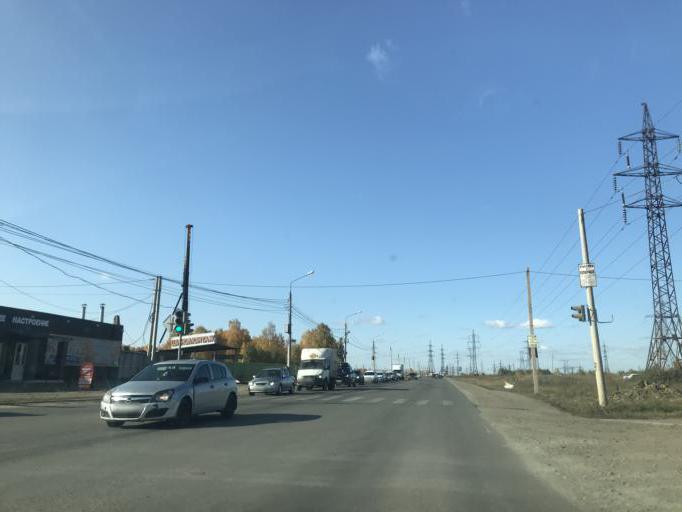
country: RU
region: Chelyabinsk
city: Roshchino
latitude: 55.2204
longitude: 61.2970
